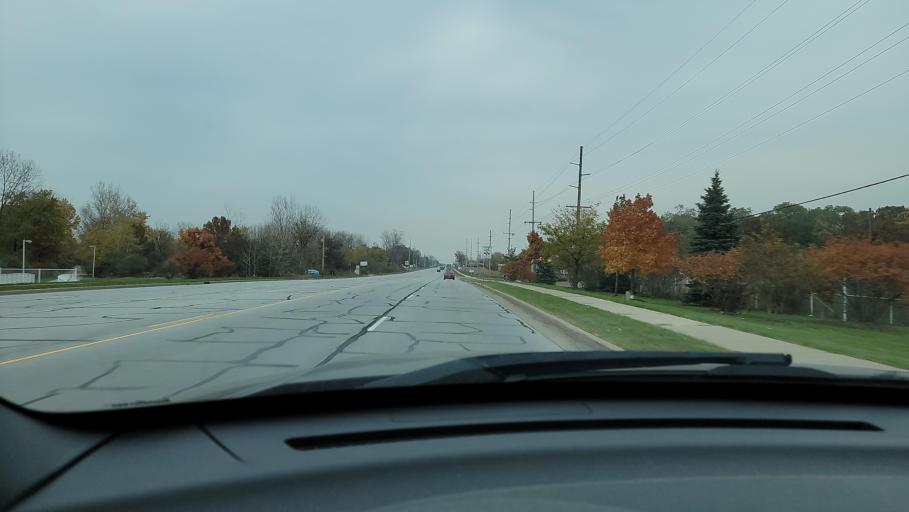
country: US
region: Indiana
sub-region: Lake County
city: Lake Station
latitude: 41.5505
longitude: -87.2135
